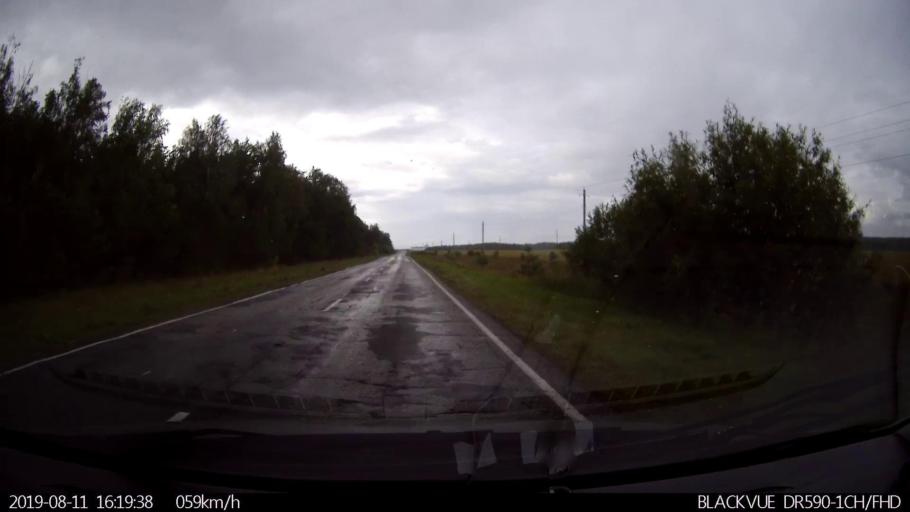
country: RU
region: Ulyanovsk
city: Mayna
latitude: 54.0654
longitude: 47.6064
